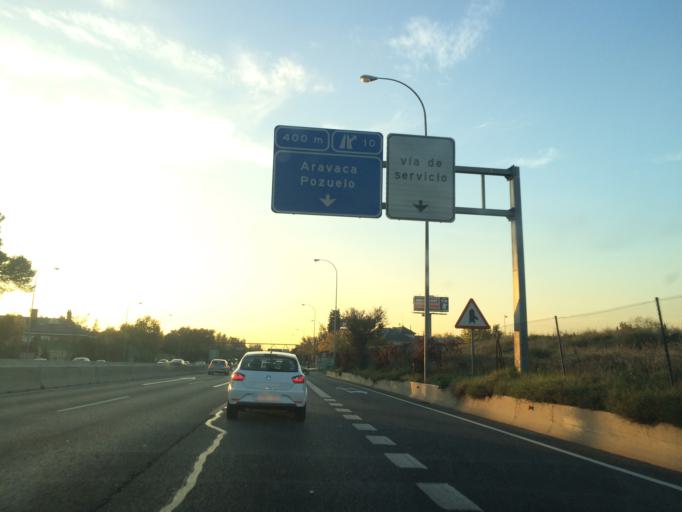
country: ES
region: Madrid
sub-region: Provincia de Madrid
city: Pozuelo de Alarcon
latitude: 40.4629
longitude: -3.7754
